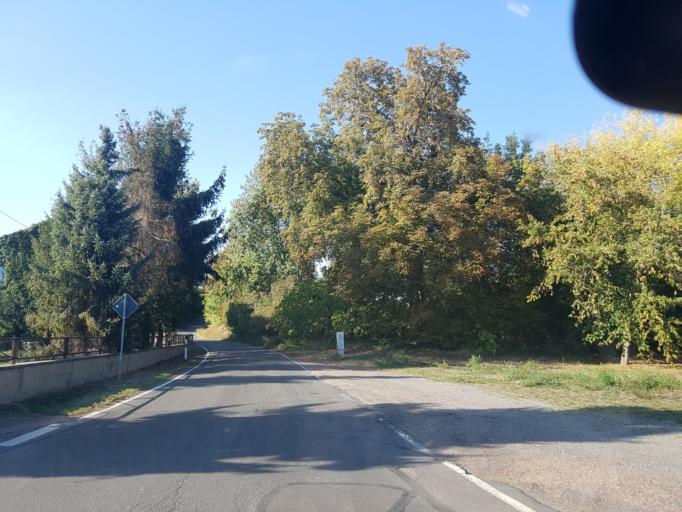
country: DE
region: Saxony
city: Ostrau
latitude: 51.1805
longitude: 13.1120
